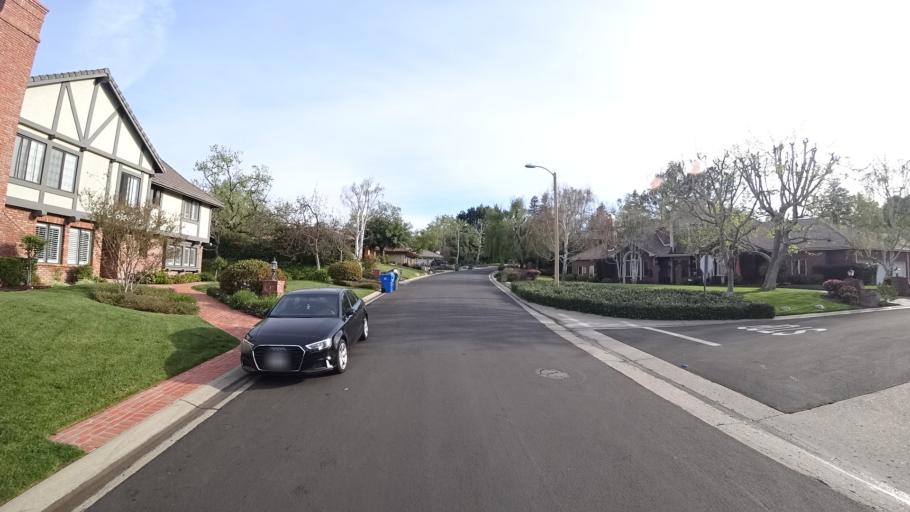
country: US
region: California
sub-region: Ventura County
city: Thousand Oaks
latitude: 34.1924
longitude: -118.8204
